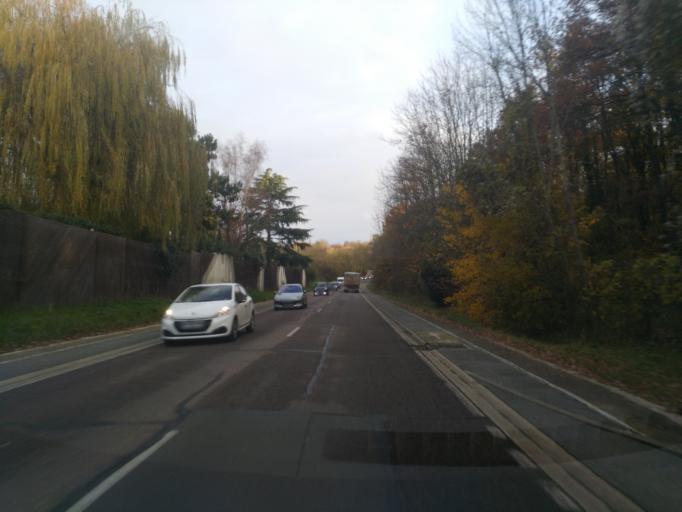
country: FR
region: Ile-de-France
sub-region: Departement des Yvelines
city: Saint-Nom-la-Breteche
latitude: 48.8607
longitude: 2.0313
